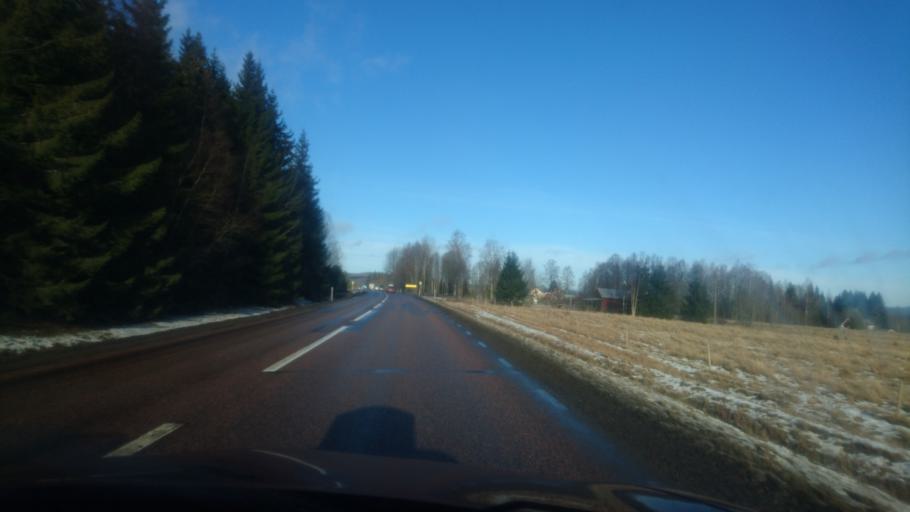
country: SE
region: Vaermland
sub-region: Sunne Kommun
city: Sunne
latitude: 59.7101
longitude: 13.1469
